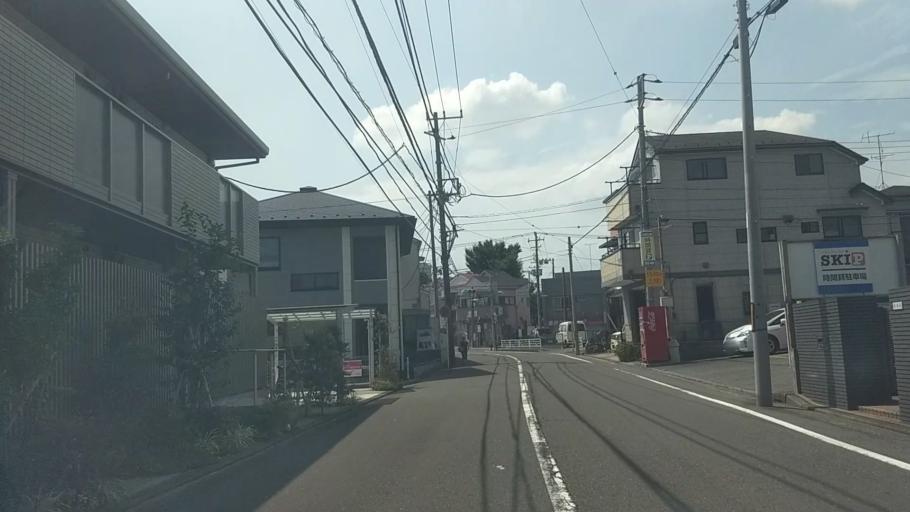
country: JP
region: Kanagawa
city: Yokohama
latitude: 35.4812
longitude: 139.6082
